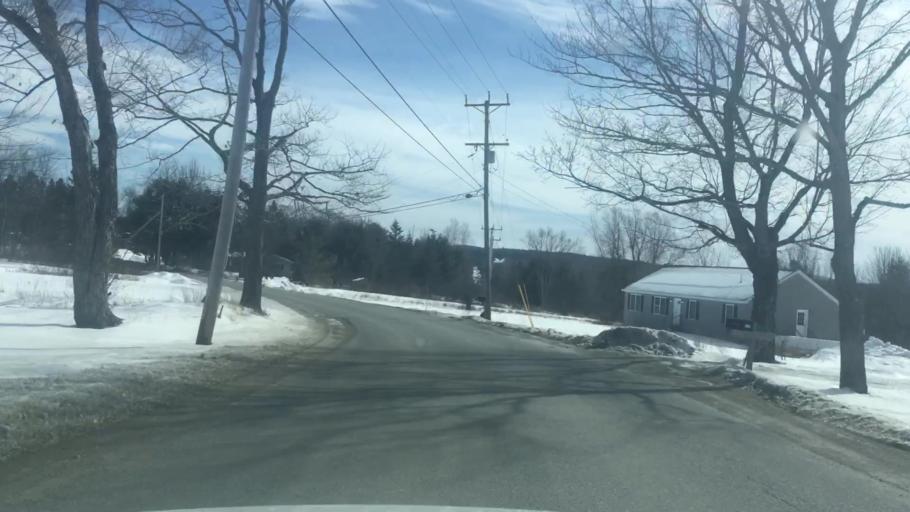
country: US
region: Maine
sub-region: Penobscot County
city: Eddington
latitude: 44.7990
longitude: -68.6785
